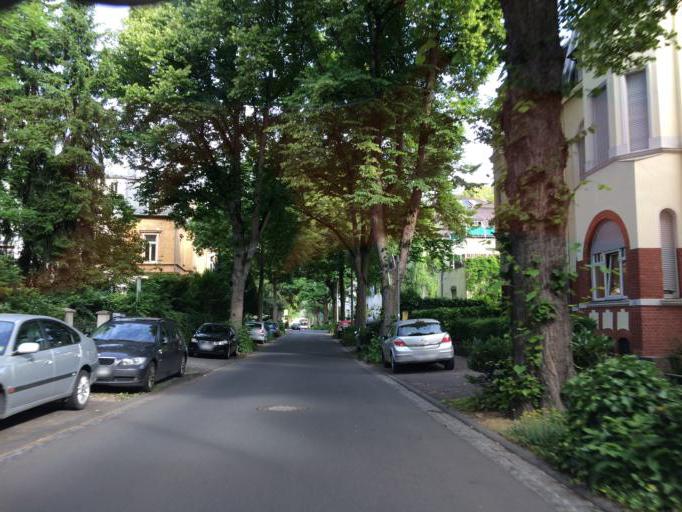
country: DE
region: North Rhine-Westphalia
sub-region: Regierungsbezirk Koln
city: Konigswinter
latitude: 50.6903
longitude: 7.1575
